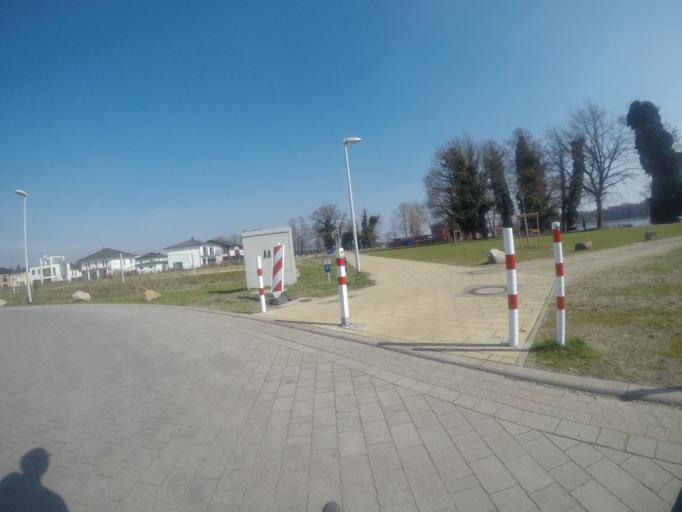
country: DE
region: Brandenburg
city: Konigs Wusterhausen
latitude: 52.2925
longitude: 13.6841
